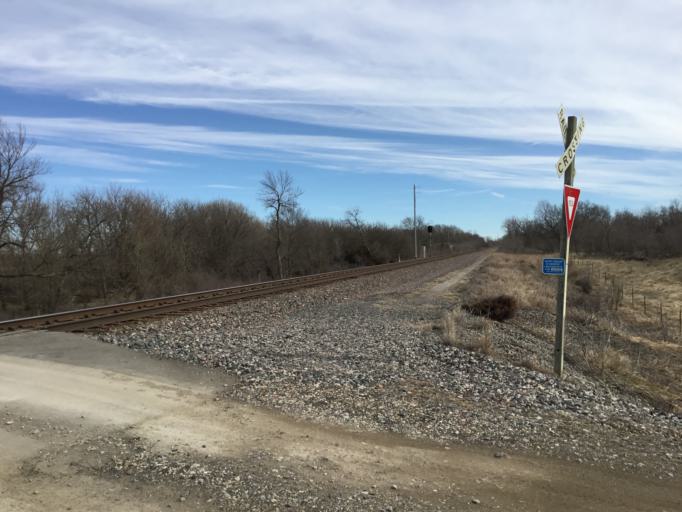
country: US
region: Kansas
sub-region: Morris County
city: Council Grove
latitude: 38.8338
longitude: -96.6316
